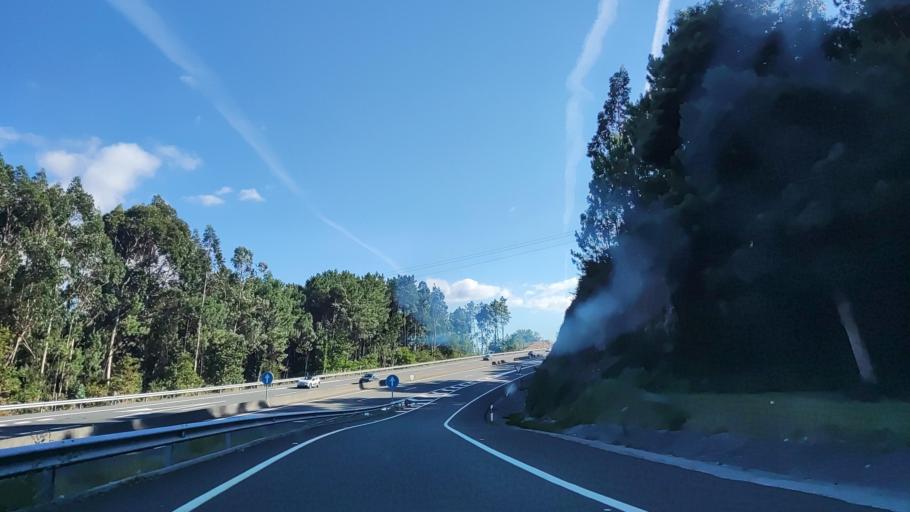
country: ES
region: Galicia
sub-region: Provincia de Pontevedra
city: Catoira
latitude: 42.7066
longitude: -8.7294
